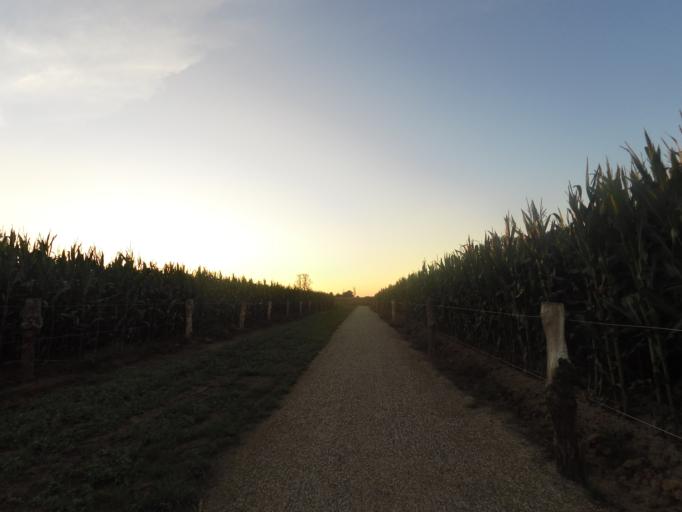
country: NL
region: Gelderland
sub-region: Oude IJsselstreek
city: Gendringen
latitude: 51.8710
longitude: 6.4096
